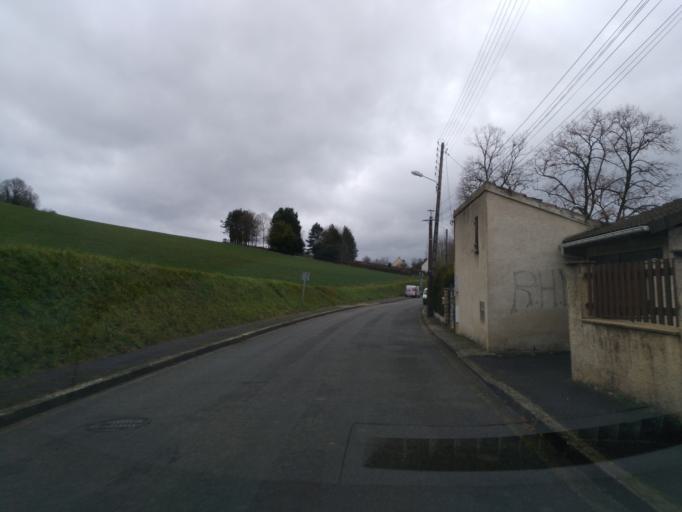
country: FR
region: Ile-de-France
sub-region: Departement des Yvelines
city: Mantes-la-Ville
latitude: 48.9509
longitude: 1.7079
